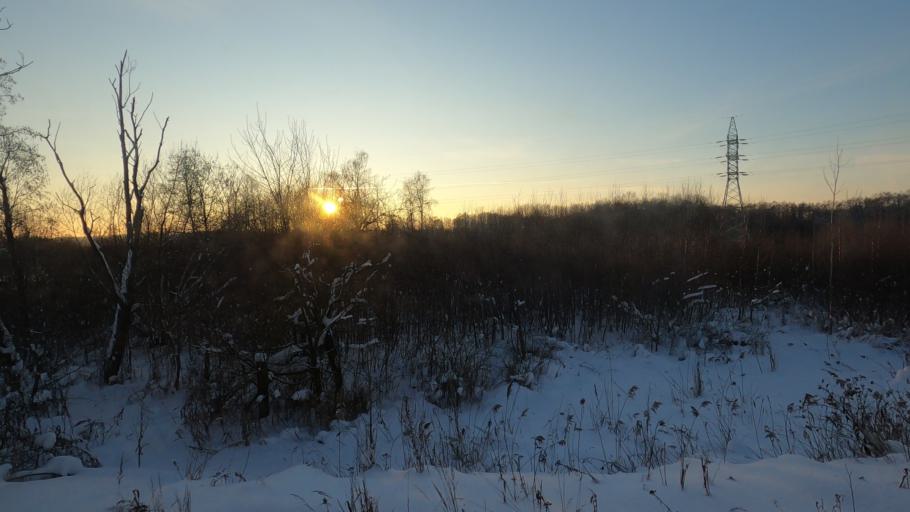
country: RU
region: Moskovskaya
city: Dmitrov
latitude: 56.3847
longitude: 37.5140
